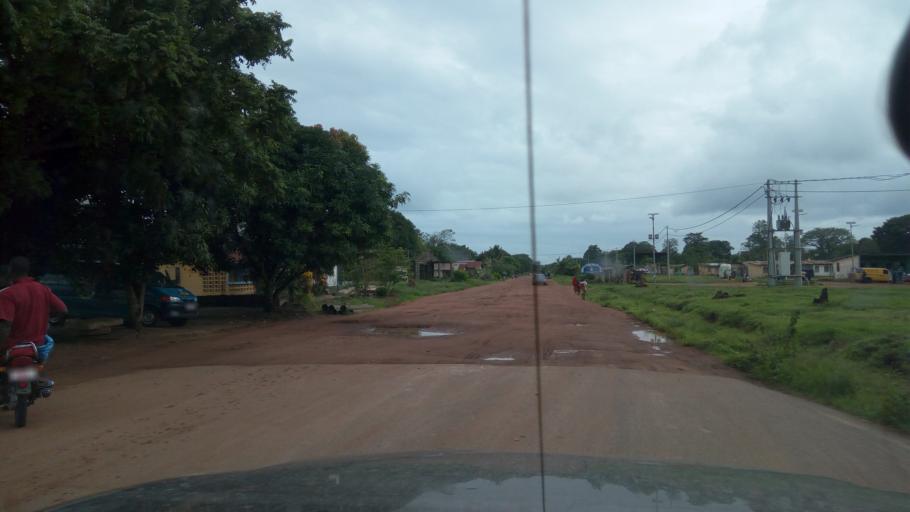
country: SL
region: Northern Province
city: Tintafor
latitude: 8.6228
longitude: -13.2138
